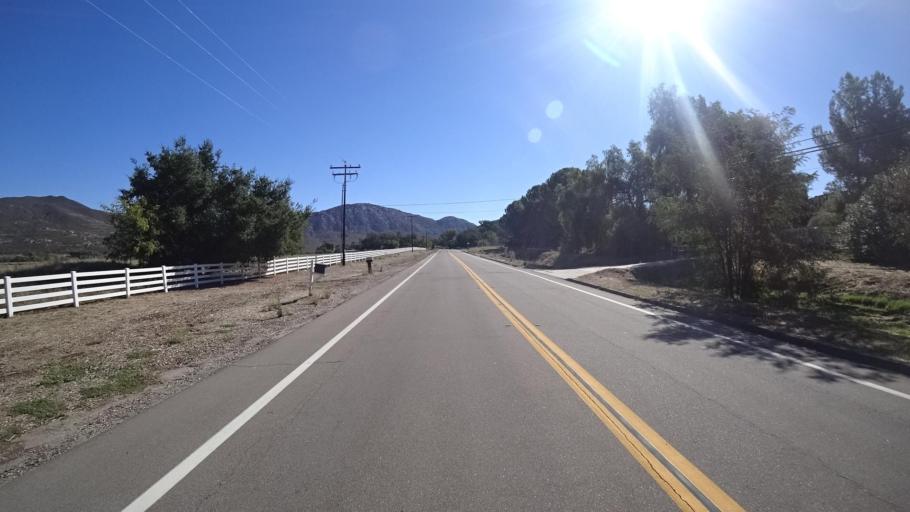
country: US
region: California
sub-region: San Diego County
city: Alpine
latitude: 32.8423
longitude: -116.6971
